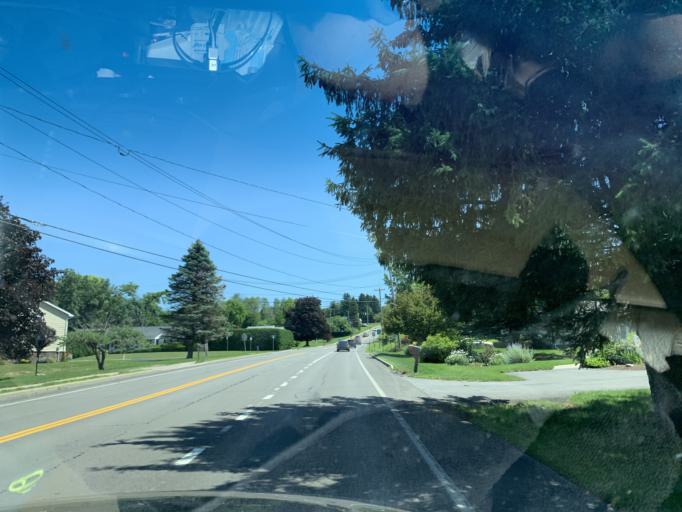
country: US
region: New York
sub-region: Oneida County
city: Washington Mills
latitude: 43.0551
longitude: -75.2603
